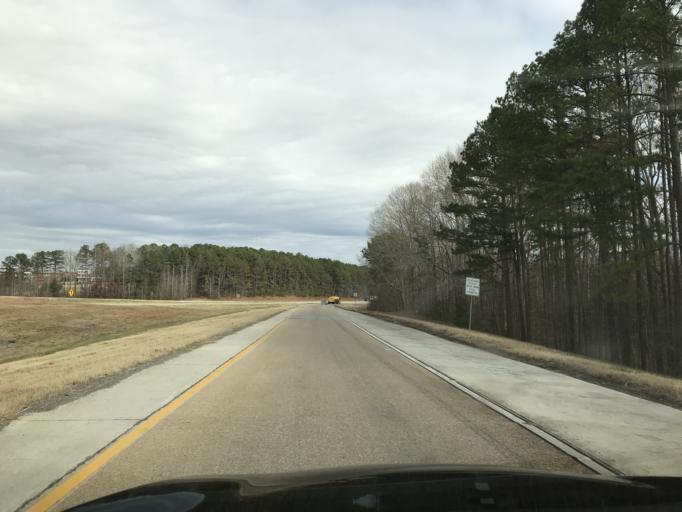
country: US
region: Georgia
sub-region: Carroll County
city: Mount Zion
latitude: 33.6878
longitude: -85.1875
